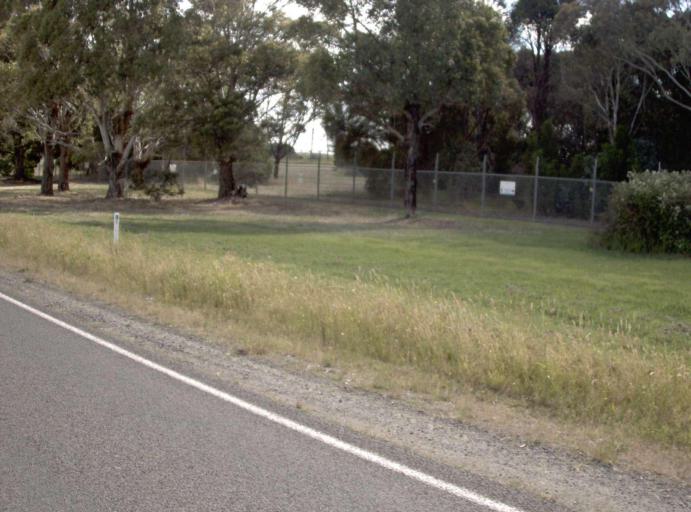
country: AU
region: Victoria
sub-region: Latrobe
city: Morwell
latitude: -38.2820
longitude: 146.4313
